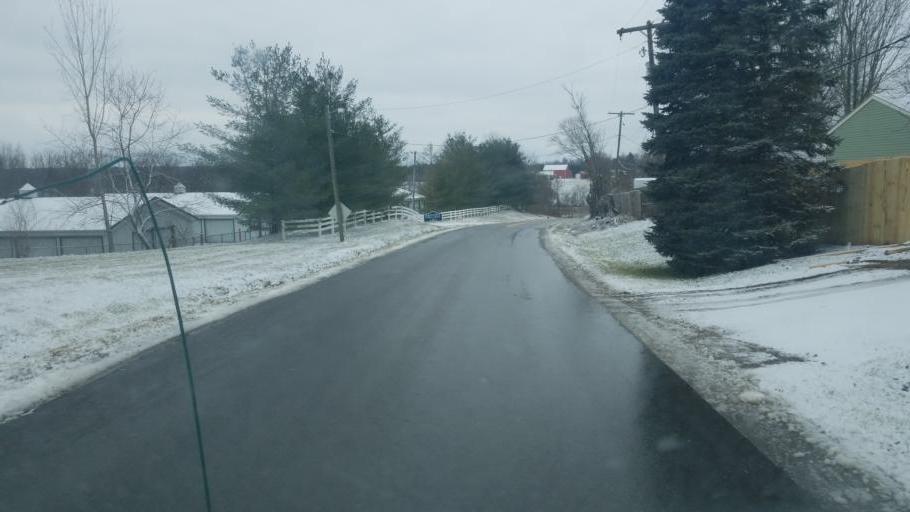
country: US
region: Ohio
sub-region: Licking County
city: Johnstown
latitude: 40.1441
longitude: -82.6890
